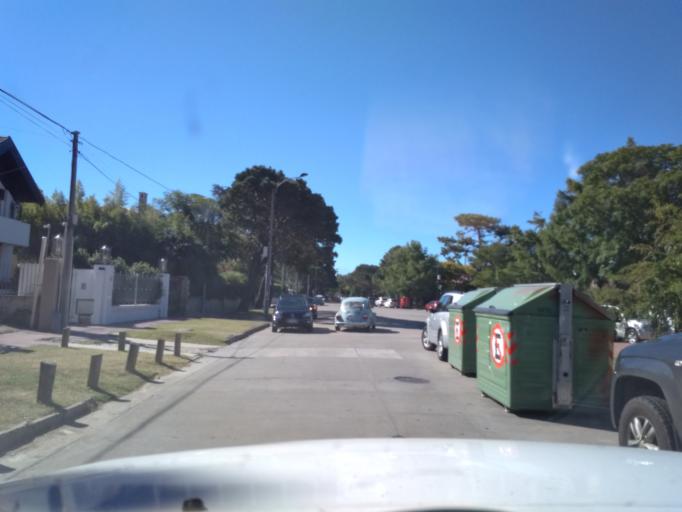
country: UY
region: Canelones
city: Paso de Carrasco
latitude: -34.8888
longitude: -56.0587
